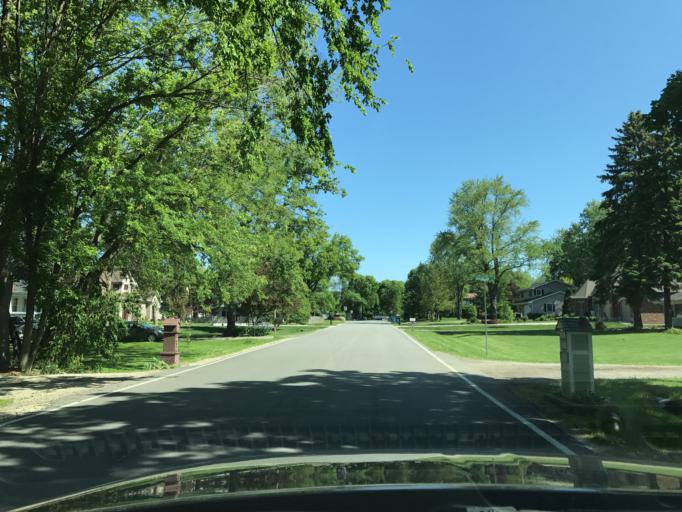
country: US
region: Illinois
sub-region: DuPage County
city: Naperville
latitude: 41.7917
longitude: -88.1369
